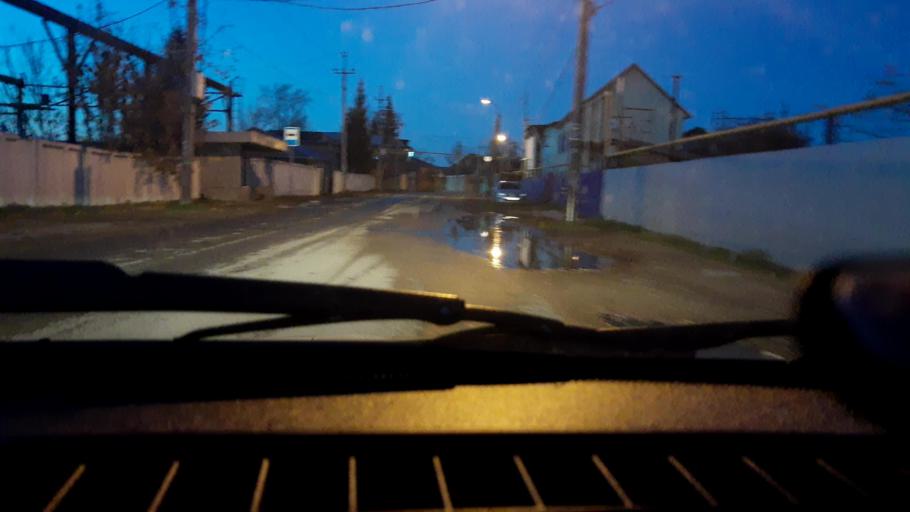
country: RU
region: Bashkortostan
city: Mikhaylovka
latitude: 54.7343
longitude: 55.8964
